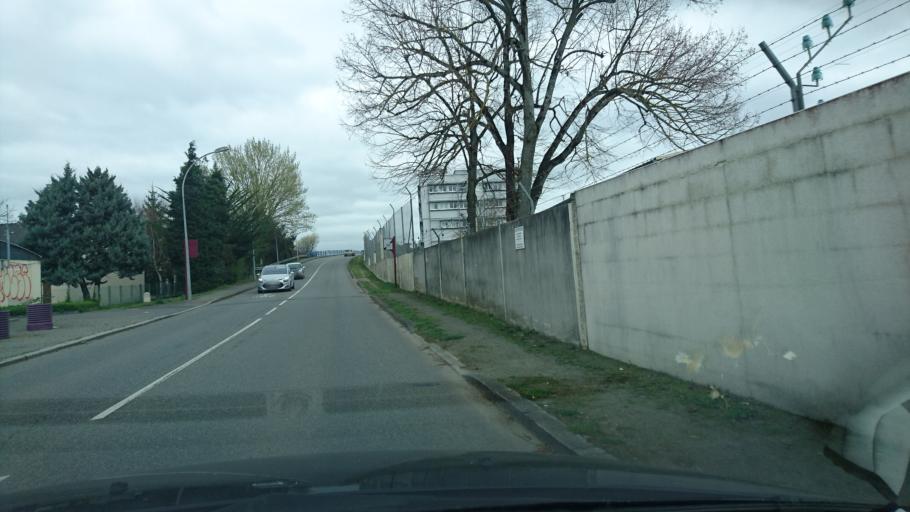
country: FR
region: Brittany
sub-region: Departement d'Ille-et-Vilaine
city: Bruz
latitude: 48.0285
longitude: -1.7498
